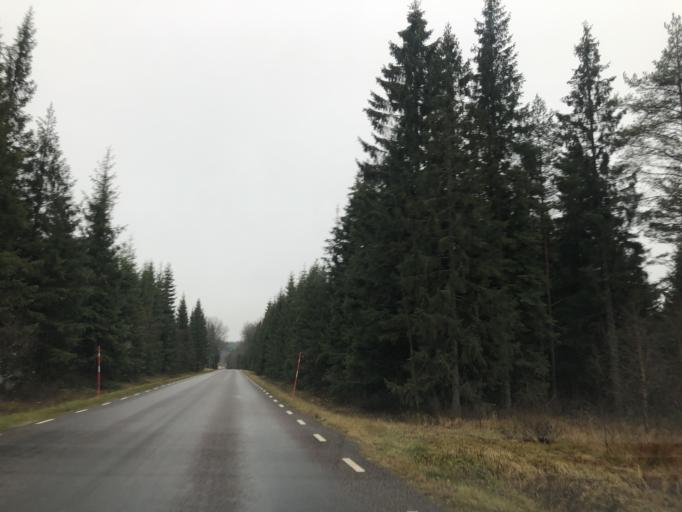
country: SE
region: Vaestra Goetaland
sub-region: Ulricehamns Kommun
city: Ulricehamn
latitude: 57.7307
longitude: 13.5453
